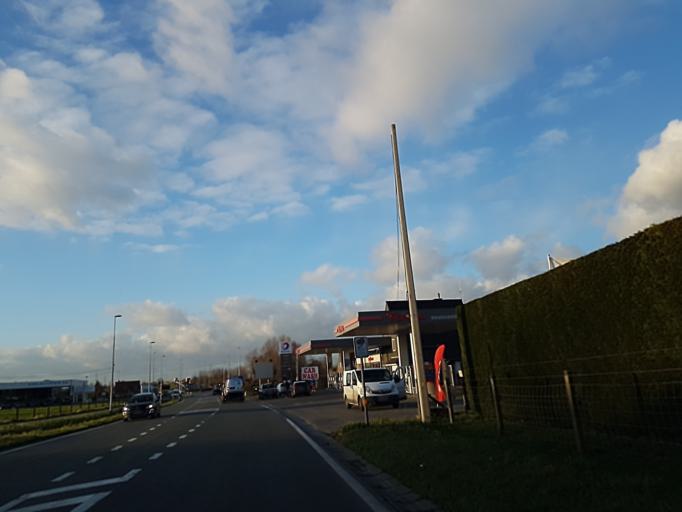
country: BE
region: Flanders
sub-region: Provincie Oost-Vlaanderen
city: Kruishoutem
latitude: 50.9121
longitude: 3.5004
